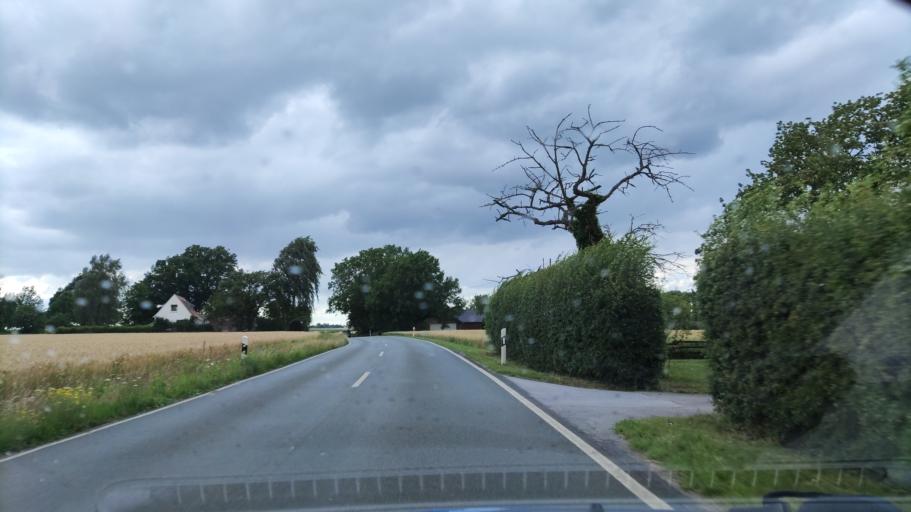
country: DE
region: North Rhine-Westphalia
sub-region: Regierungsbezirk Arnsberg
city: Soest
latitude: 51.5925
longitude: 8.0755
